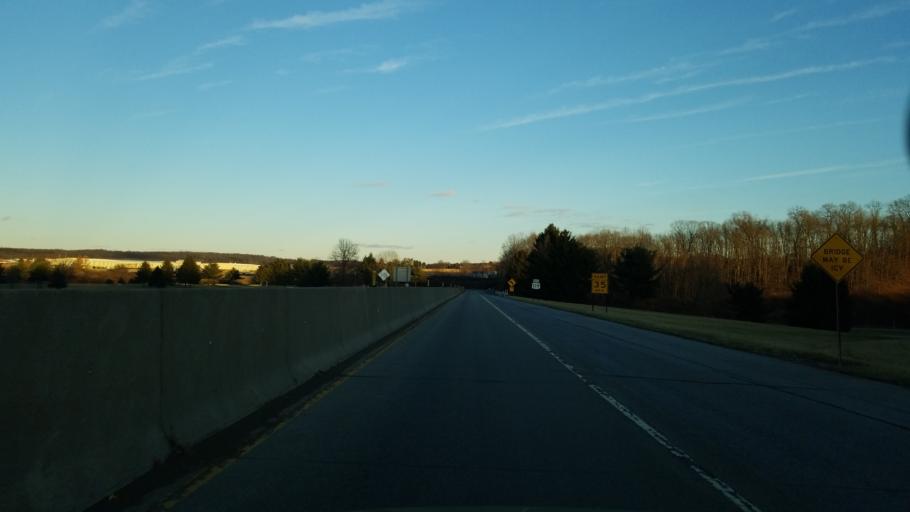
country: US
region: Pennsylvania
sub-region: Indiana County
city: Chevy Chase Heights
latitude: 40.6265
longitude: -79.1198
